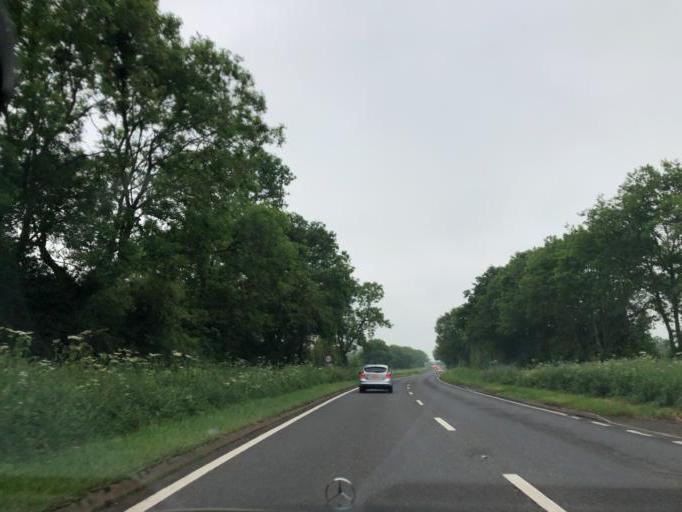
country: GB
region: England
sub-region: Warwickshire
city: Harbury
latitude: 52.2150
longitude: -1.5132
